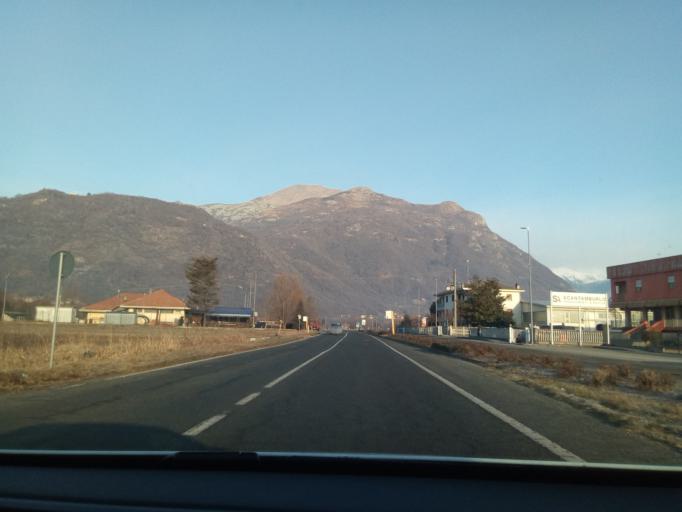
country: IT
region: Piedmont
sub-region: Provincia di Torino
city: Fiorano Canavese
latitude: 45.4765
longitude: 7.8331
